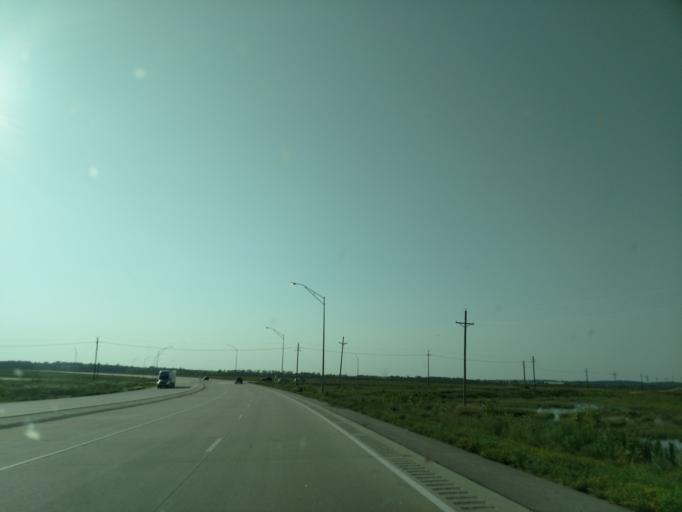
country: US
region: Nebraska
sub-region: Sarpy County
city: Offutt Air Force Base
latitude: 41.0755
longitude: -95.8893
